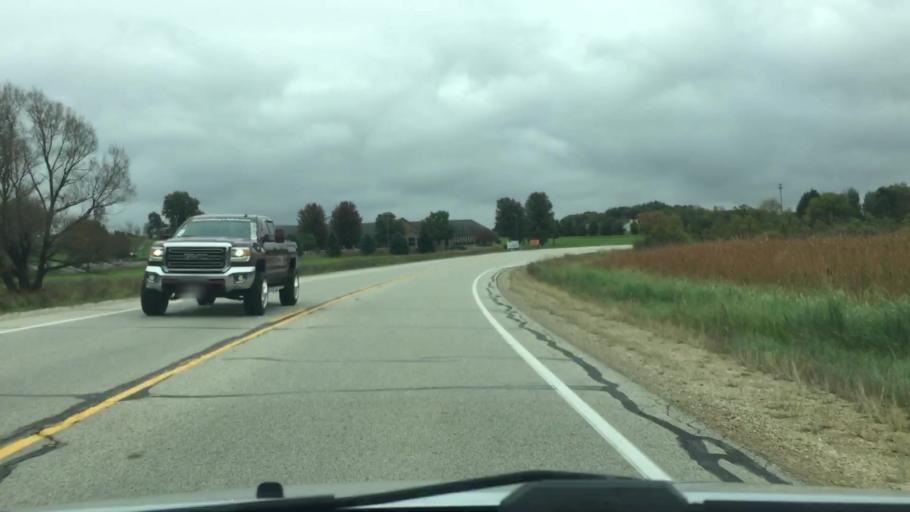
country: US
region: Wisconsin
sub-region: Walworth County
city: Elkhorn
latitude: 42.7336
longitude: -88.5441
